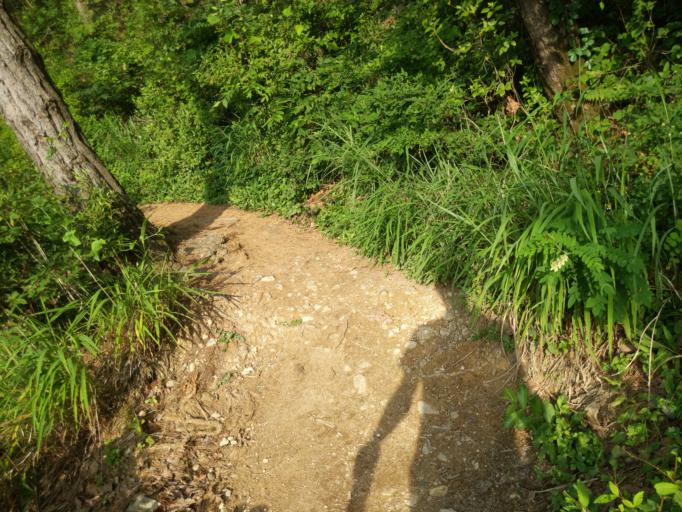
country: KR
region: Daegu
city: Hwawon
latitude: 35.7865
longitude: 128.5446
